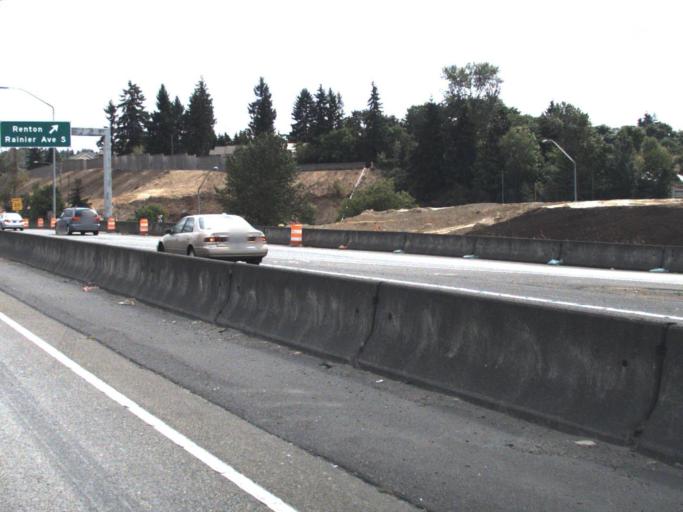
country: US
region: Washington
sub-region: King County
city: Renton
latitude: 47.4677
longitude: -122.2190
